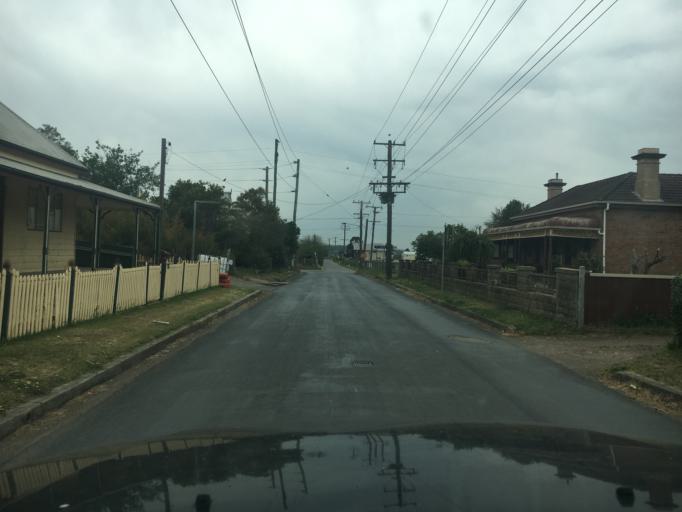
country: AU
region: New South Wales
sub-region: Maitland Municipality
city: Maitland
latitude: -32.7494
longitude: 151.5587
